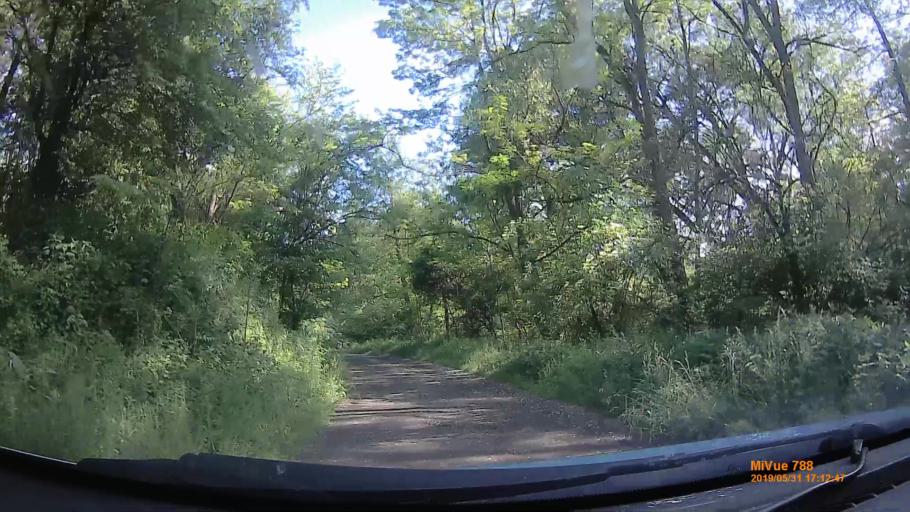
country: HU
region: Nograd
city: Nagyoroszi
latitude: 48.0375
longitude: 19.0466
